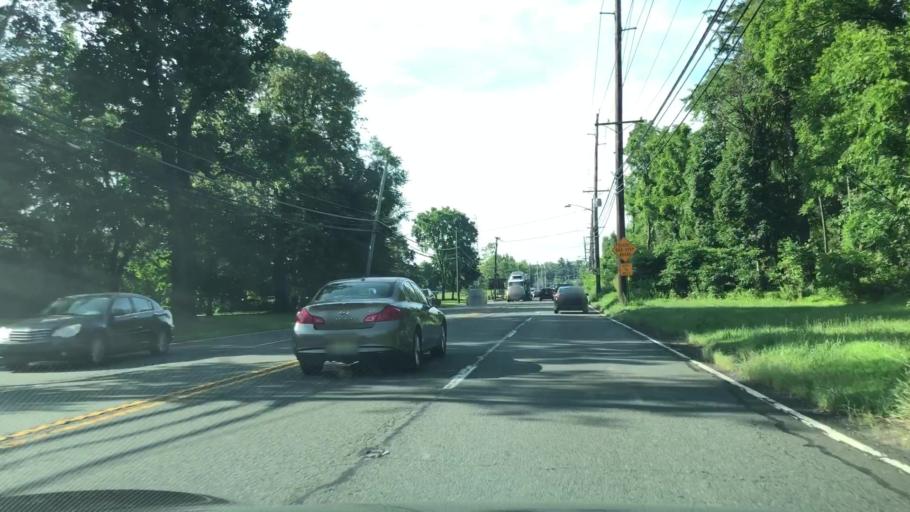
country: US
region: New Jersey
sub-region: Mercer County
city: Pennington
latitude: 40.3040
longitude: -74.7845
